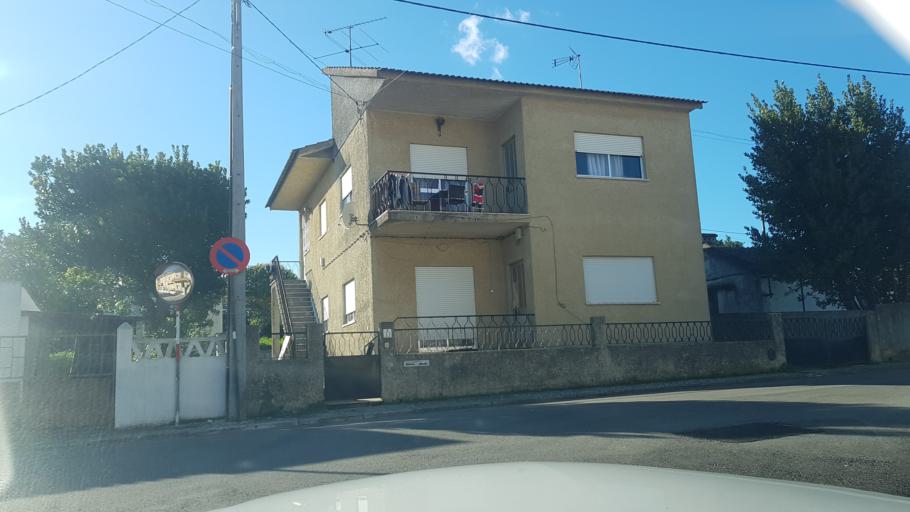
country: PT
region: Santarem
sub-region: Entroncamento
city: Entroncamento
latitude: 39.4741
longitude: -8.4792
